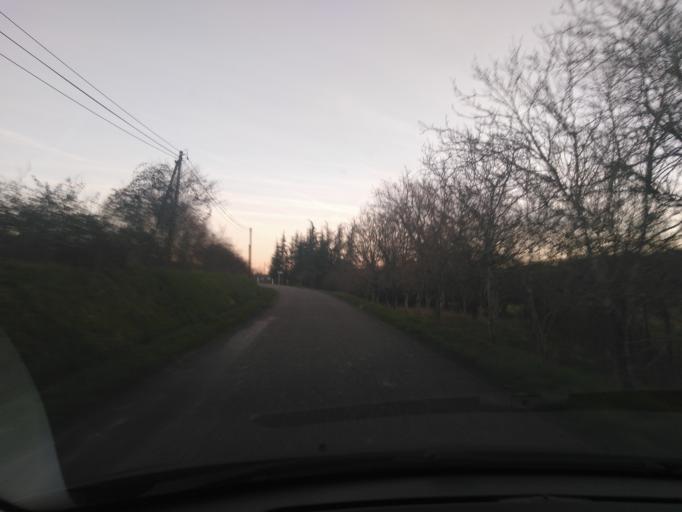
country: FR
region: Aquitaine
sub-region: Departement du Lot-et-Garonne
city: Saint-Hilaire
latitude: 44.4886
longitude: 0.6997
